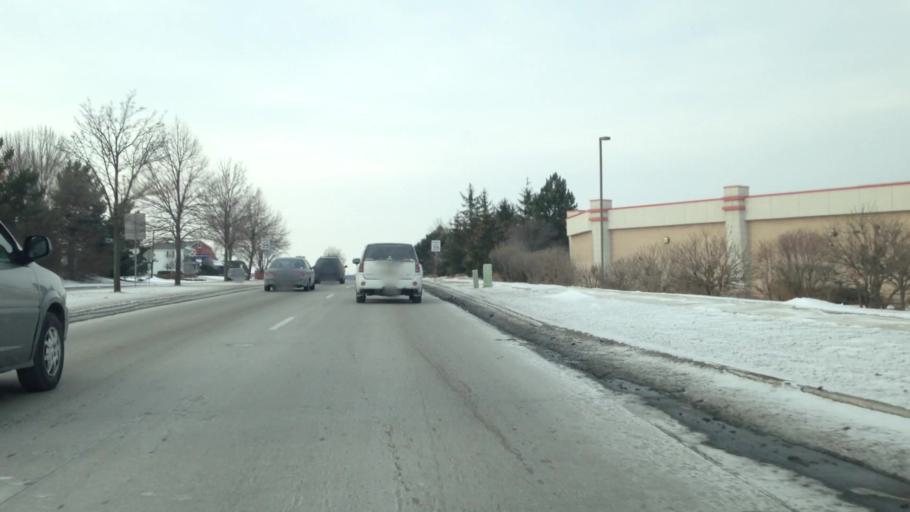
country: US
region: Wisconsin
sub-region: Waukesha County
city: Menomonee Falls
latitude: 43.1875
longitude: -88.1291
